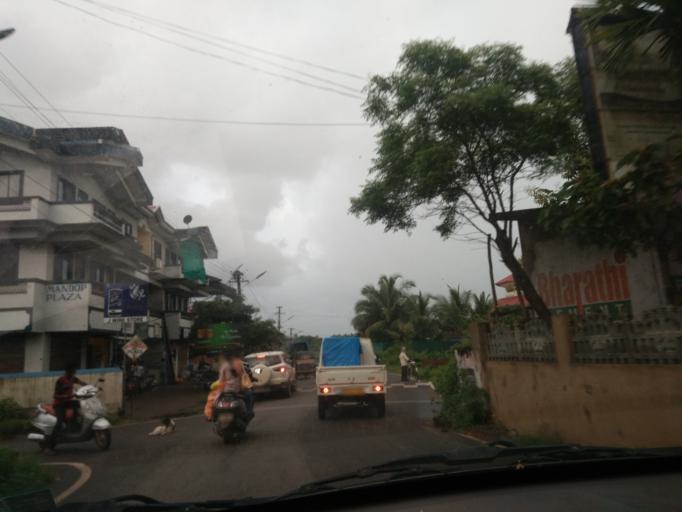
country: IN
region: Goa
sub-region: South Goa
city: Davorlim
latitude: 15.2509
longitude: 73.9793
